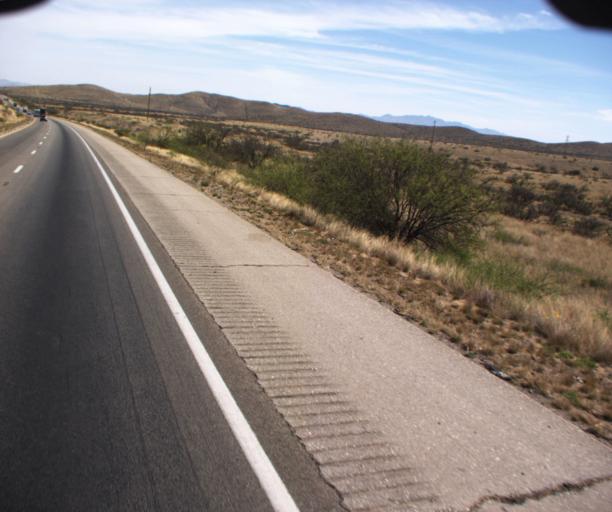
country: US
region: Arizona
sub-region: Cochise County
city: Saint David
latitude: 32.0908
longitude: -110.0381
